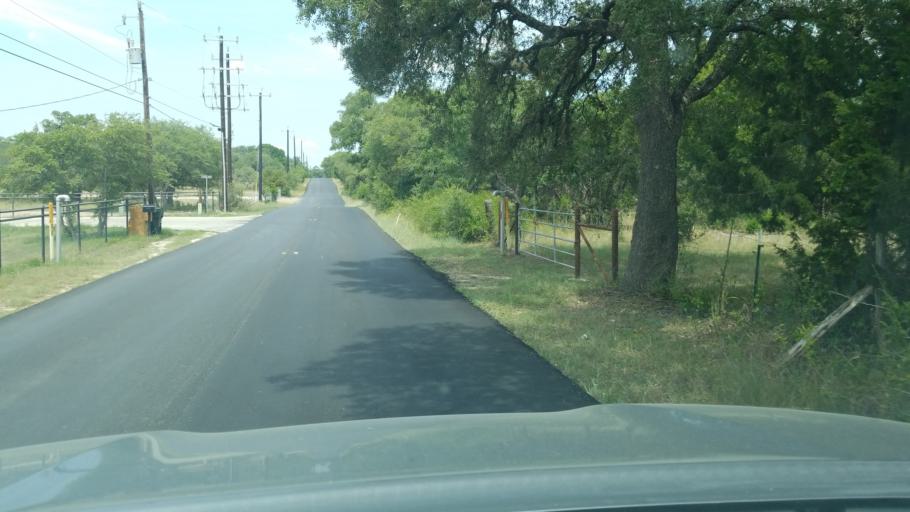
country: US
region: Texas
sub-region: Comal County
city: Bulverde
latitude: 29.7598
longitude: -98.4764
